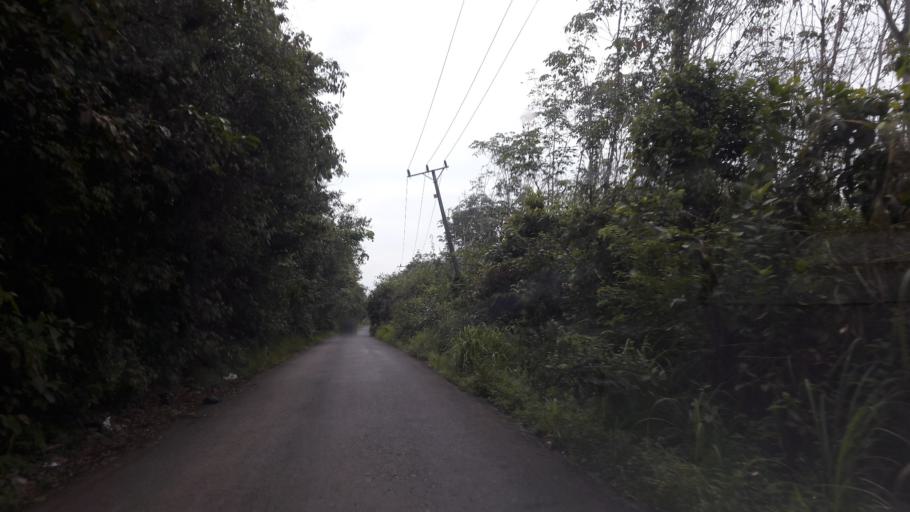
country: ID
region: South Sumatra
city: Gunungmenang
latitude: -3.1273
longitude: 104.1103
